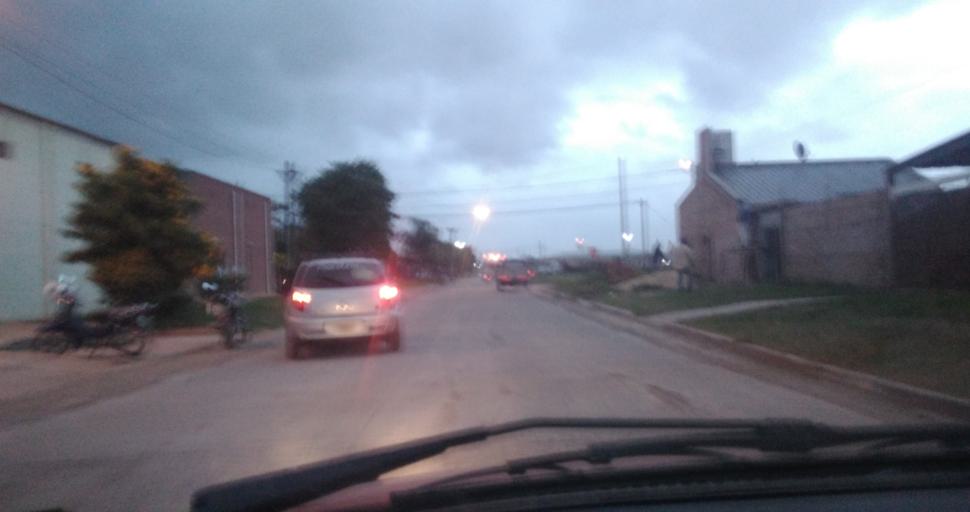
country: AR
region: Chaco
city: Fontana
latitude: -27.4184
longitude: -59.0421
